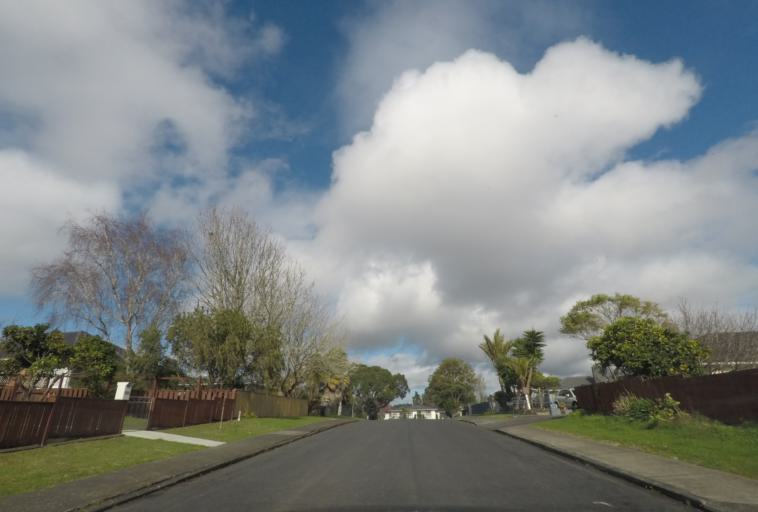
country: NZ
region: Auckland
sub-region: Auckland
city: Rosebank
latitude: -36.8951
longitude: 174.6624
